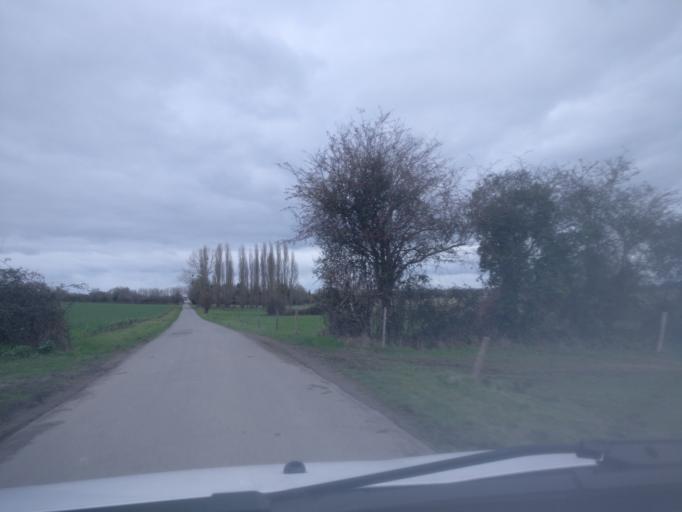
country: FR
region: Lower Normandy
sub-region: Departement de la Manche
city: Marcey-les-Greves
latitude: 48.6602
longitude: -1.4378
